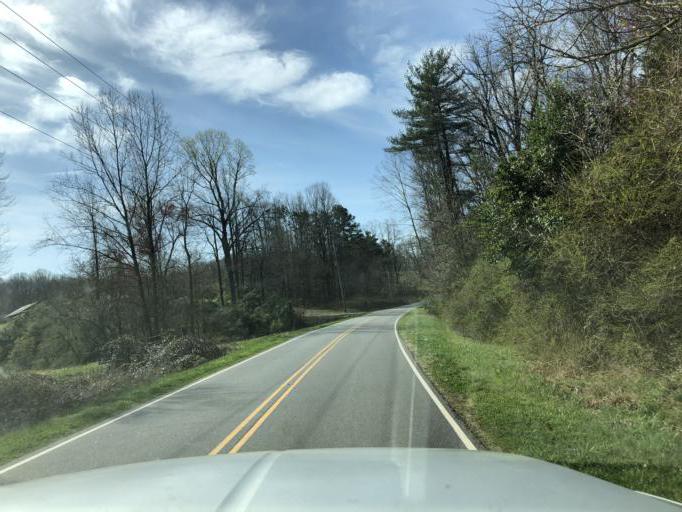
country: US
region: North Carolina
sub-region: Cleveland County
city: Shelby
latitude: 35.4335
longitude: -81.6409
